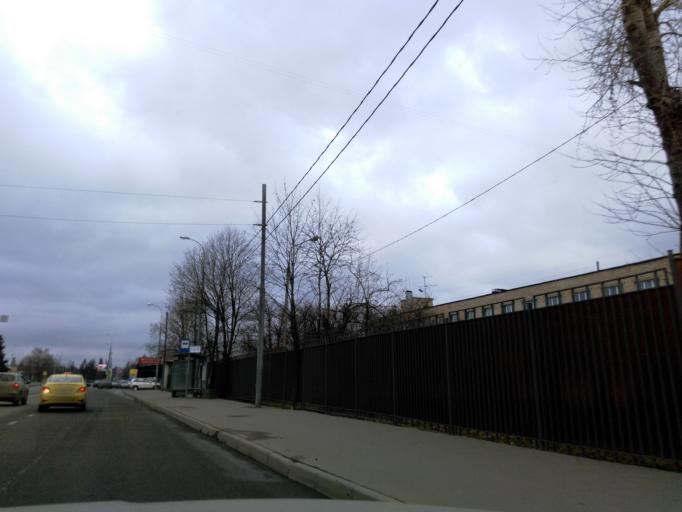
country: RU
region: Moskovskaya
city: Rzhavki
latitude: 55.9809
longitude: 37.2544
